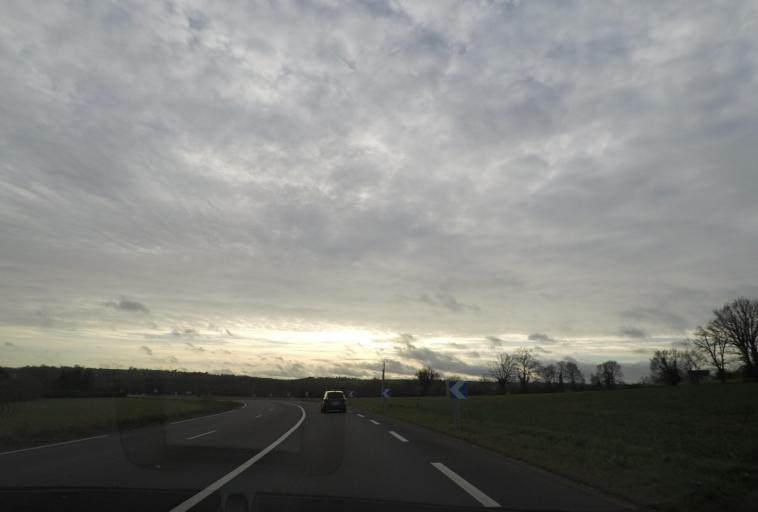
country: FR
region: Centre
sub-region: Departement du Loir-et-Cher
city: Sarge-sur-Braye
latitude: 47.9146
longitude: 0.8327
